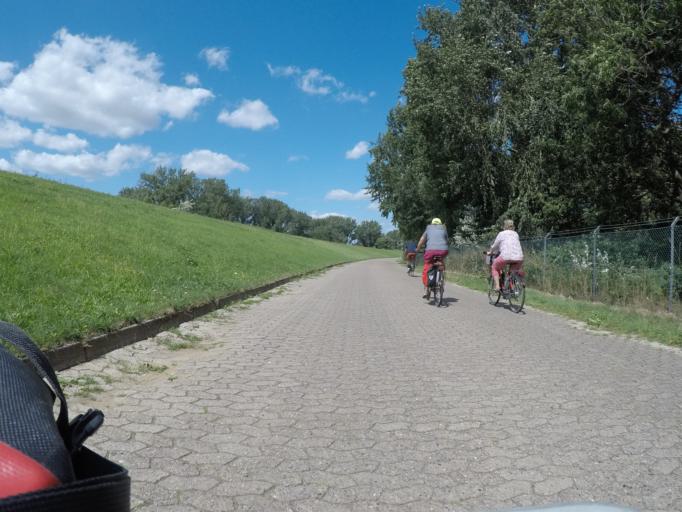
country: DE
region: Hamburg
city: Rothenburgsort
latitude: 53.5030
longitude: 10.0654
